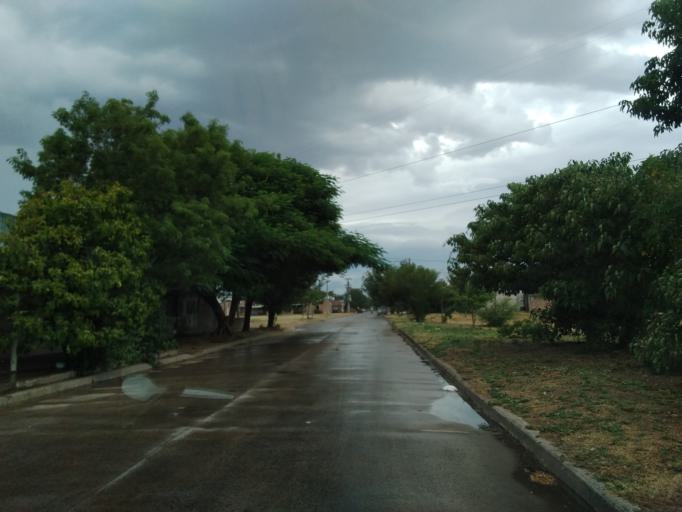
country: AR
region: Corrientes
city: Corrientes
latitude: -27.5177
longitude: -58.7893
